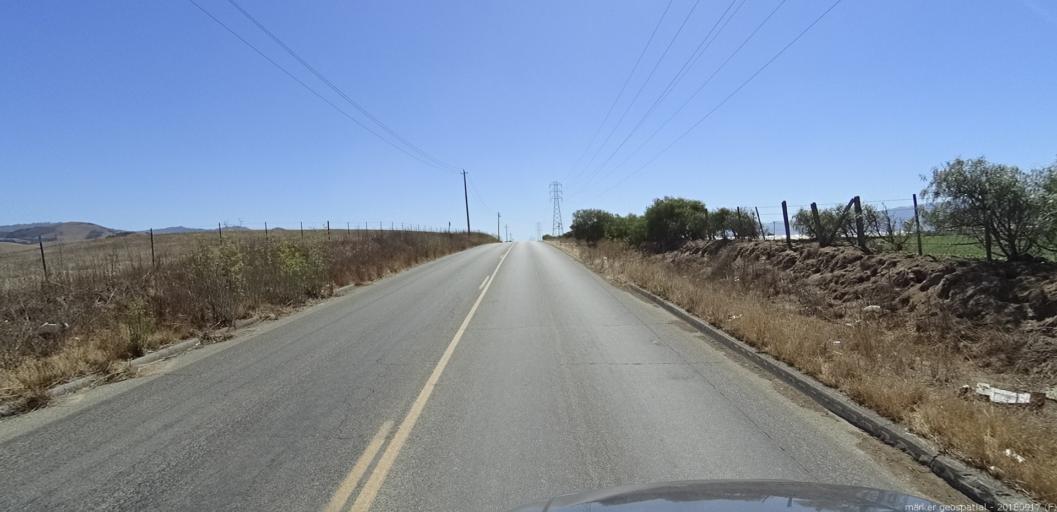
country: US
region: California
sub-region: Monterey County
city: Salinas
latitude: 36.7166
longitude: -121.5910
